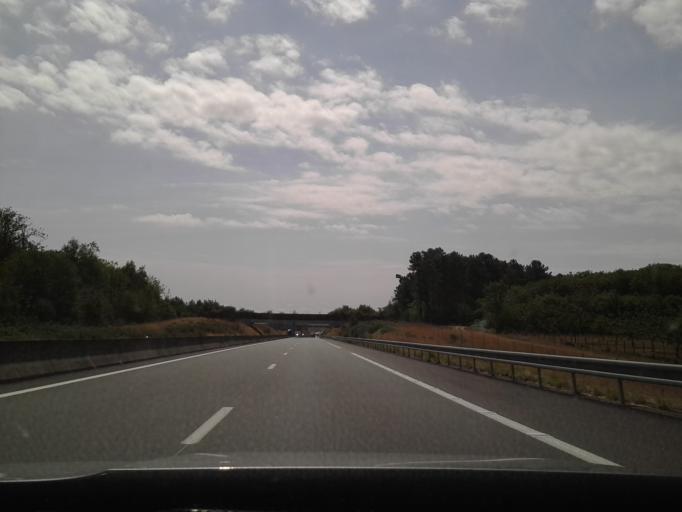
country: FR
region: Pays de la Loire
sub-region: Departement de la Sarthe
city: Luceau
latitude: 47.6981
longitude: 0.3564
